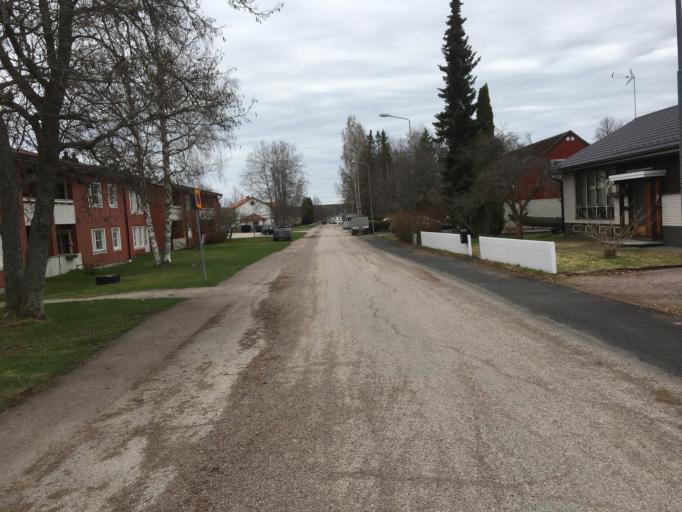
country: SE
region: Gaevleborg
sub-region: Hofors Kommun
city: Hofors
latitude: 60.5139
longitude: 16.4683
